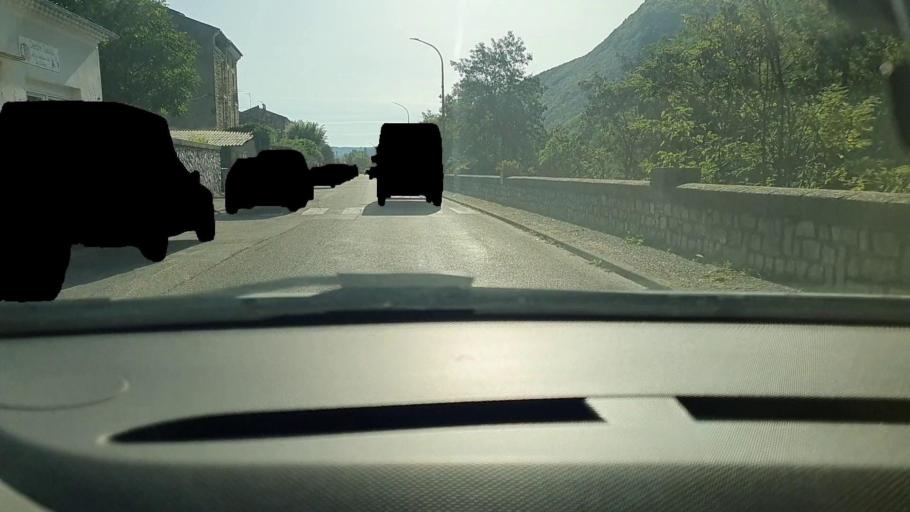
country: FR
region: Languedoc-Roussillon
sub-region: Departement du Gard
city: Besseges
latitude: 44.2916
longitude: 4.0962
